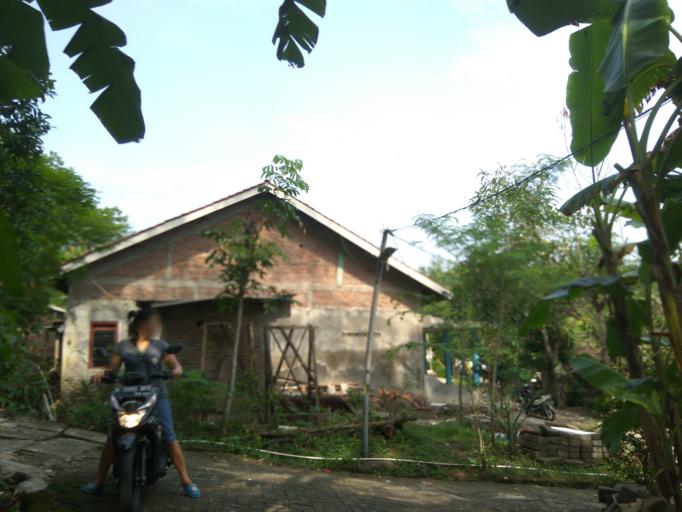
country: ID
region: Central Java
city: Semarang
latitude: -7.0363
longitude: 110.4086
